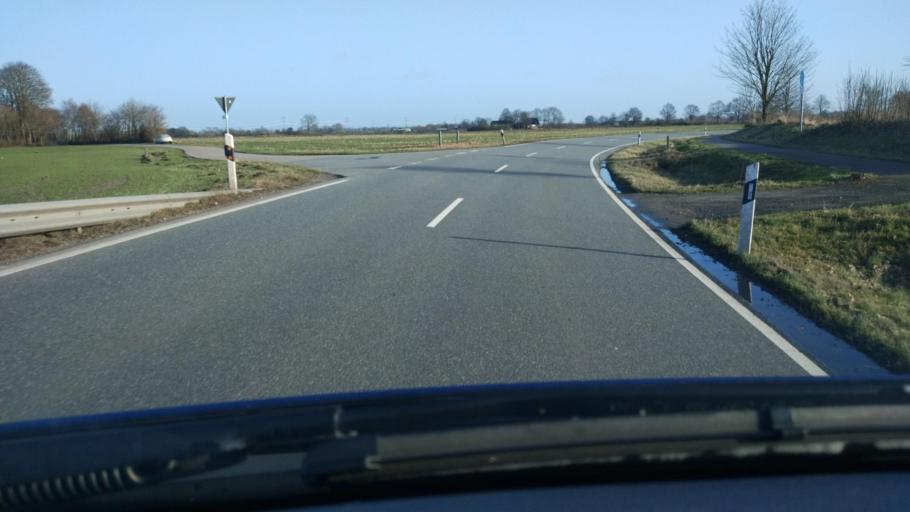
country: DE
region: Schleswig-Holstein
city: Wanderup
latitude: 54.6895
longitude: 9.3565
